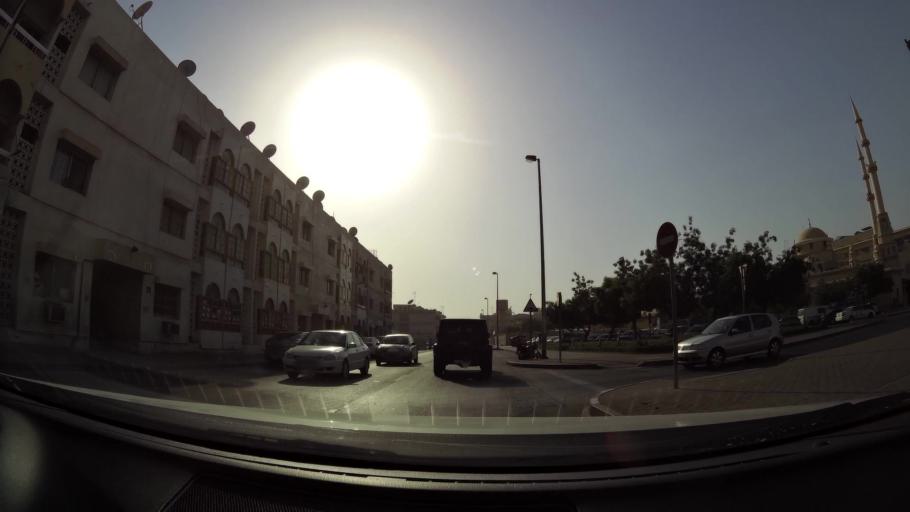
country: AE
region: Ash Shariqah
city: Sharjah
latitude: 25.2434
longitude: 55.3029
